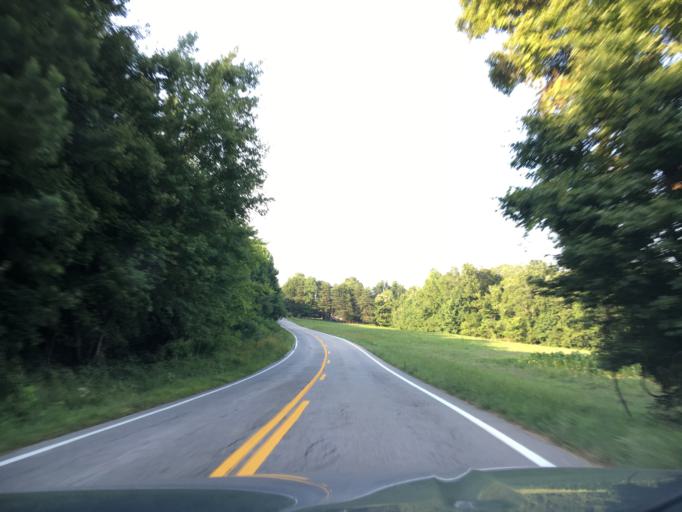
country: US
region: Virginia
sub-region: Pittsylvania County
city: Chatham
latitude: 36.8223
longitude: -79.2531
